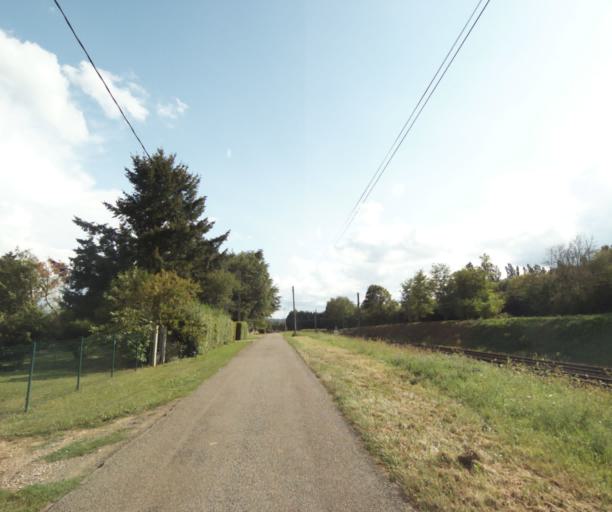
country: FR
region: Bourgogne
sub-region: Departement de Saone-et-Loire
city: Tournus
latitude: 46.5781
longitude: 4.9053
